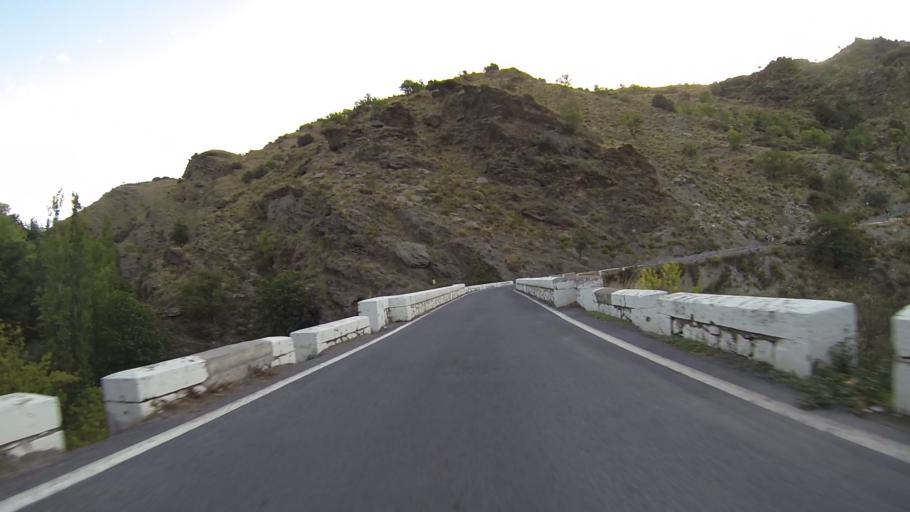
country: ES
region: Andalusia
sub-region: Provincia de Granada
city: Berchules
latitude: 36.9887
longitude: -3.1503
